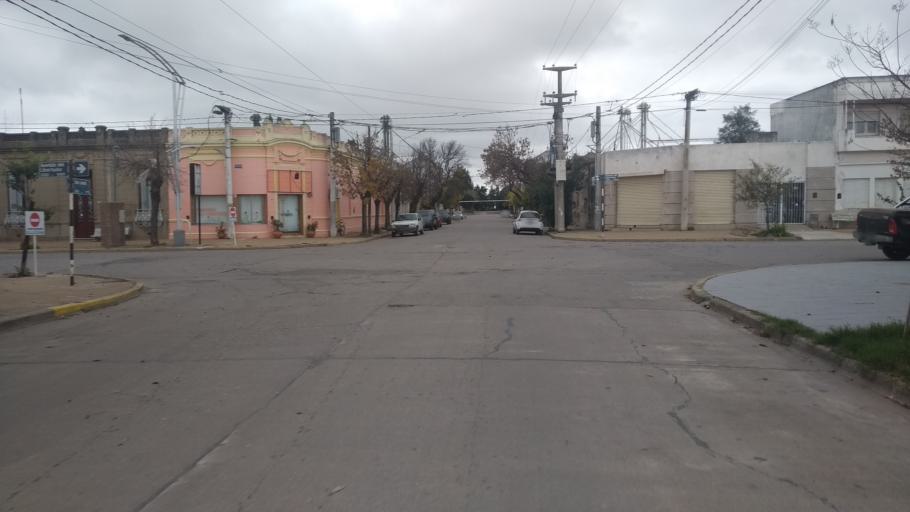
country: AR
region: Cordoba
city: Leones
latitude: -32.6614
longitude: -62.3027
